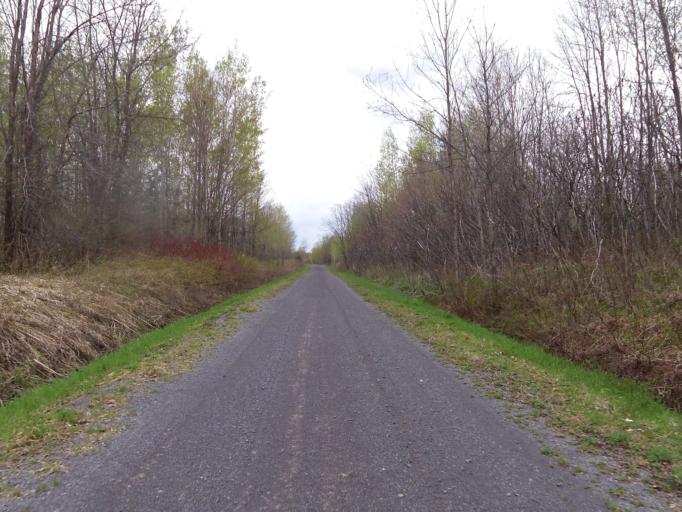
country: CA
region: Quebec
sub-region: Outaouais
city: Papineauville
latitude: 45.5192
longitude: -74.9639
